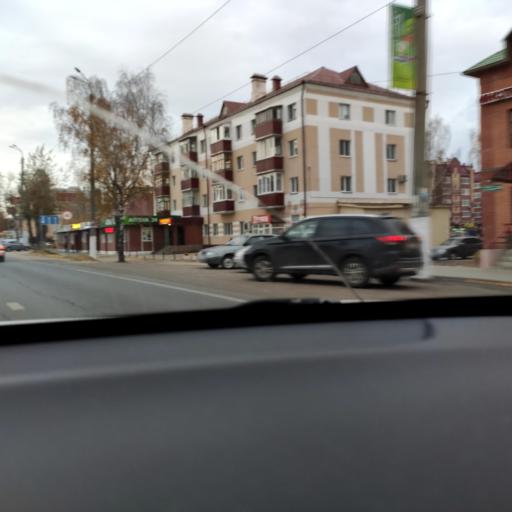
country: RU
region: Tatarstan
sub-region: Zelenodol'skiy Rayon
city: Zelenodolsk
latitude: 55.8479
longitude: 48.5593
